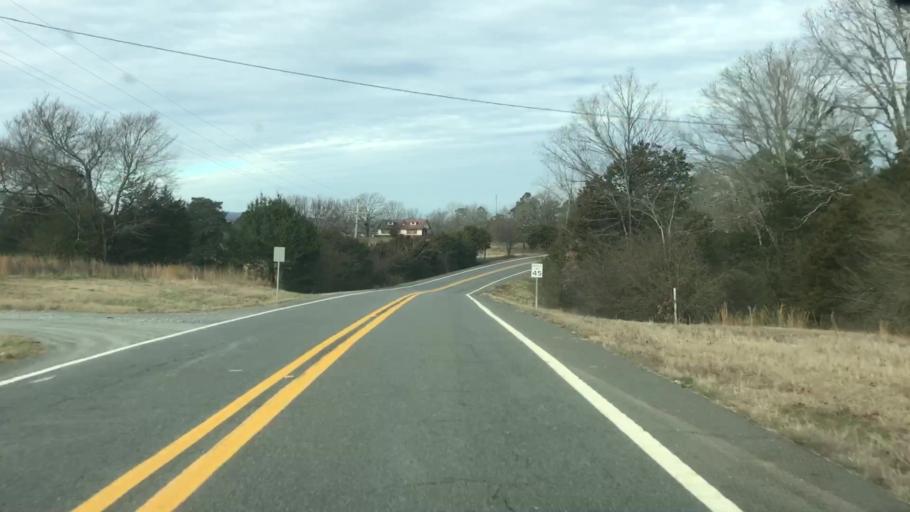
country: US
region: Arkansas
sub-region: Montgomery County
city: Mount Ida
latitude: 34.6245
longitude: -93.7286
